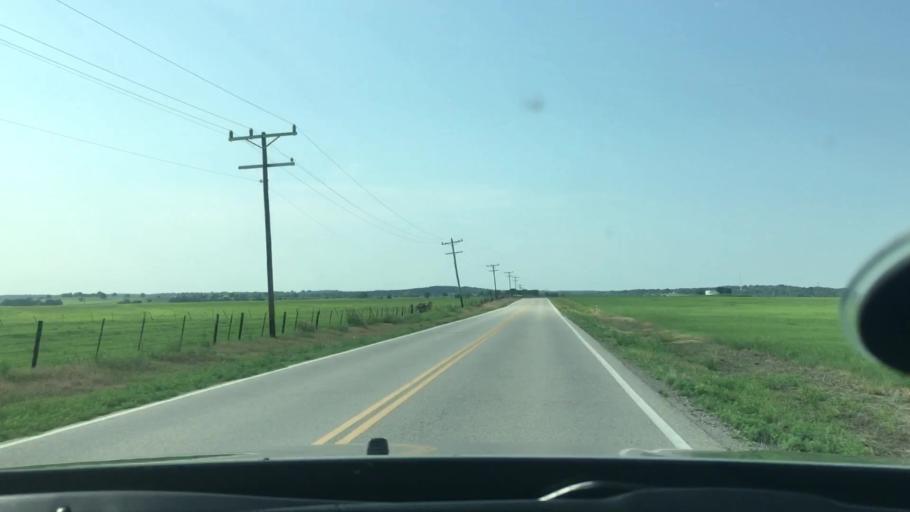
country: US
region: Oklahoma
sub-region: Bryan County
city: Durant
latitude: 34.1079
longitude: -96.4877
